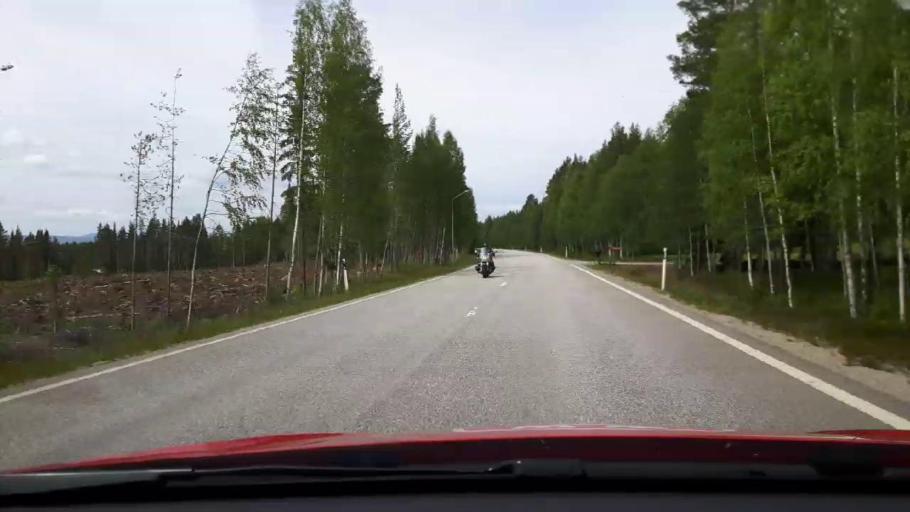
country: SE
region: Jaemtland
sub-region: Harjedalens Kommun
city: Sveg
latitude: 62.1234
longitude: 14.1589
